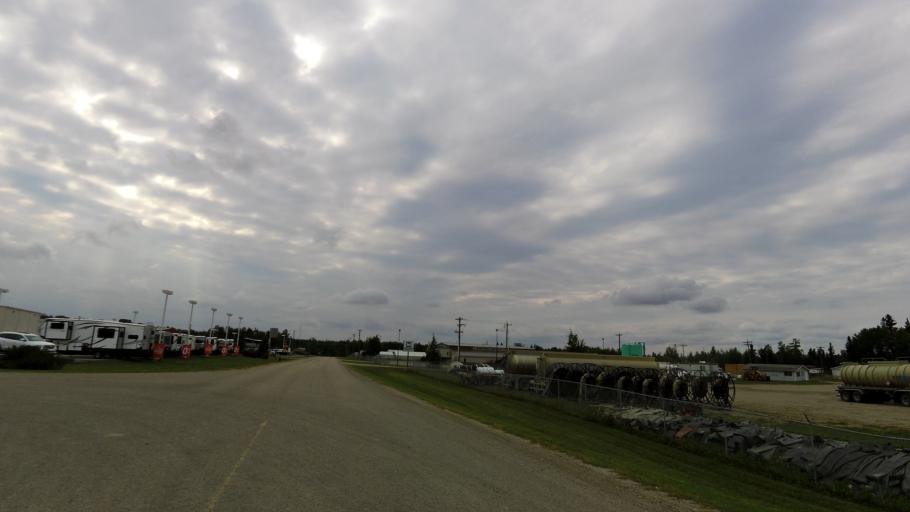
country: CA
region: Alberta
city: Rocky Mountain House
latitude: 52.3631
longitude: -114.9074
